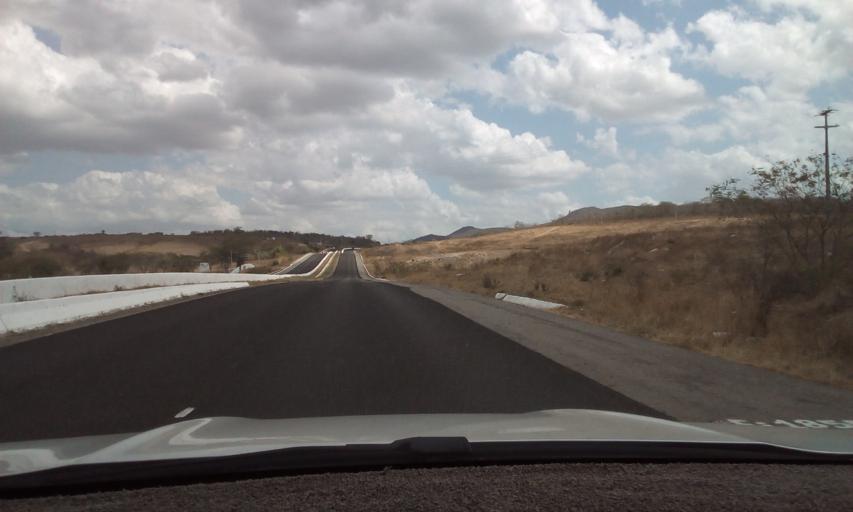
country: BR
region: Pernambuco
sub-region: Toritama
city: Toritama
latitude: -8.0612
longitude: -36.0477
